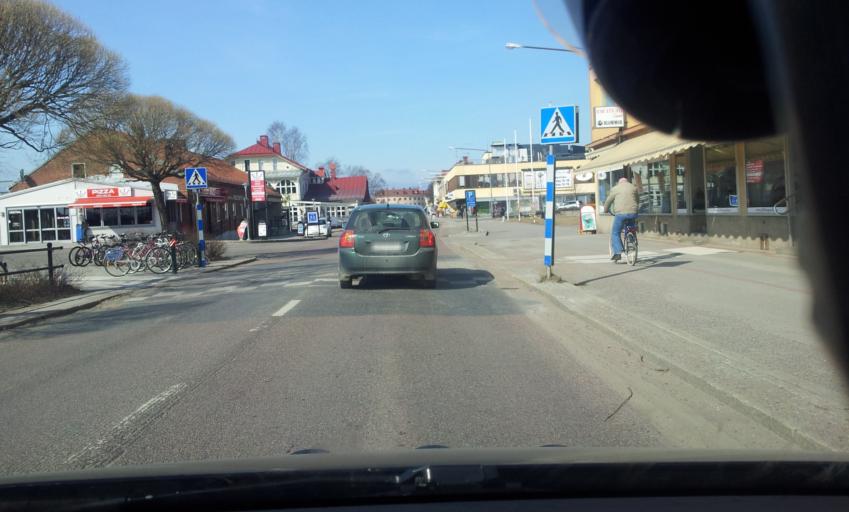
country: SE
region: Gaevleborg
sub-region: Ljusdals Kommun
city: Ljusdal
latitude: 61.8269
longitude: 16.0981
